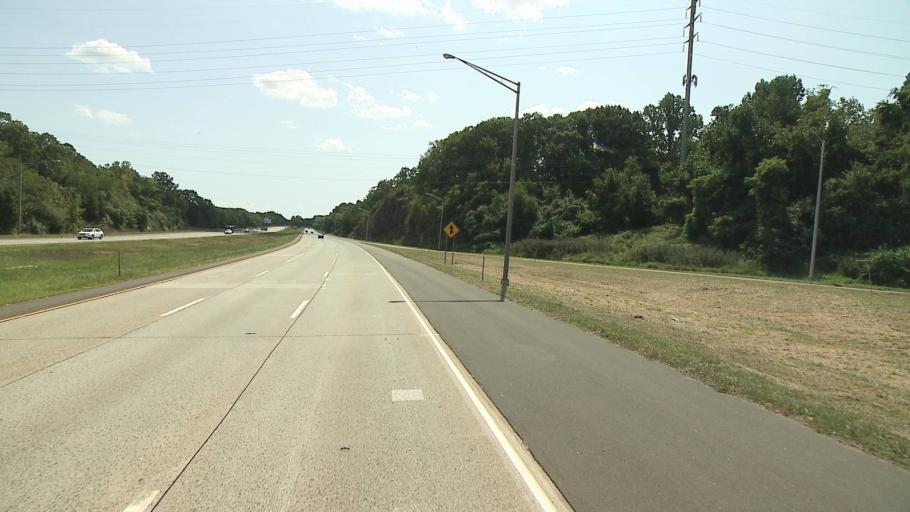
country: US
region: Connecticut
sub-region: Fairfield County
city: Trumbull
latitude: 41.2325
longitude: -73.1897
